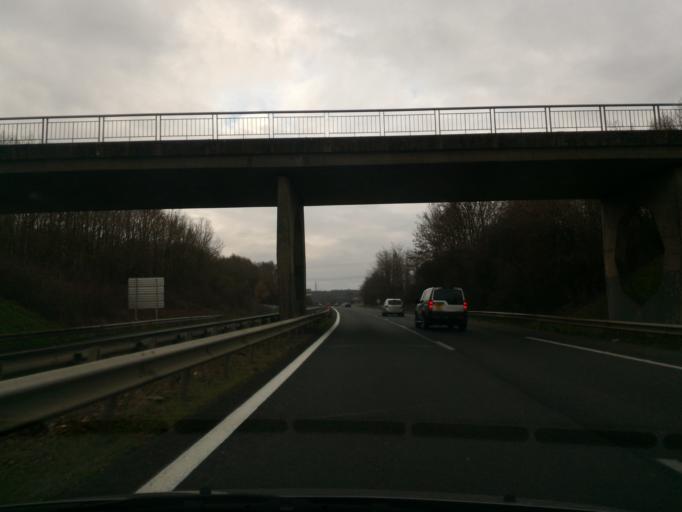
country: FR
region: Poitou-Charentes
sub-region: Departement de la Vienne
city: Celle-Levescault
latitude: 46.3692
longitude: 0.2085
